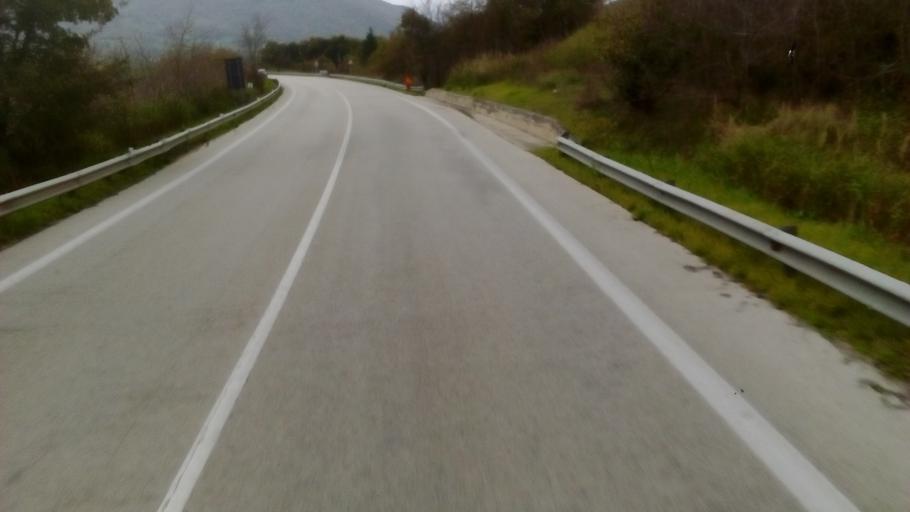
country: IT
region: Abruzzo
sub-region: Provincia di Chieti
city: Celenza sul Trigno
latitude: 41.8755
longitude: 14.6038
